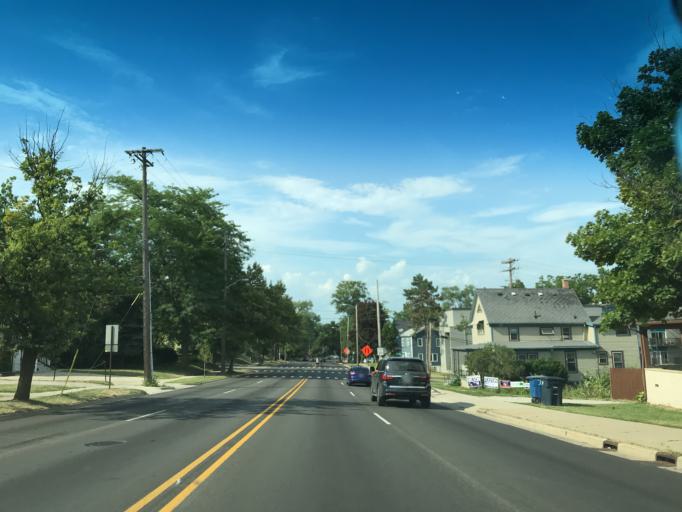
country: US
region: Michigan
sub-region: Washtenaw County
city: Ann Arbor
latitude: 42.2685
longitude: -83.7502
